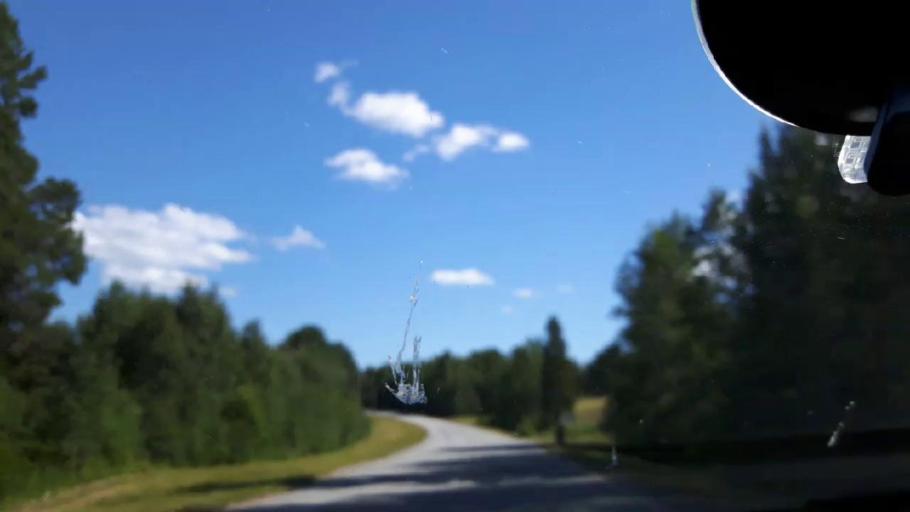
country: SE
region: Vaesternorrland
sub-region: Ange Kommun
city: Fransta
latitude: 62.7048
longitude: 16.3633
